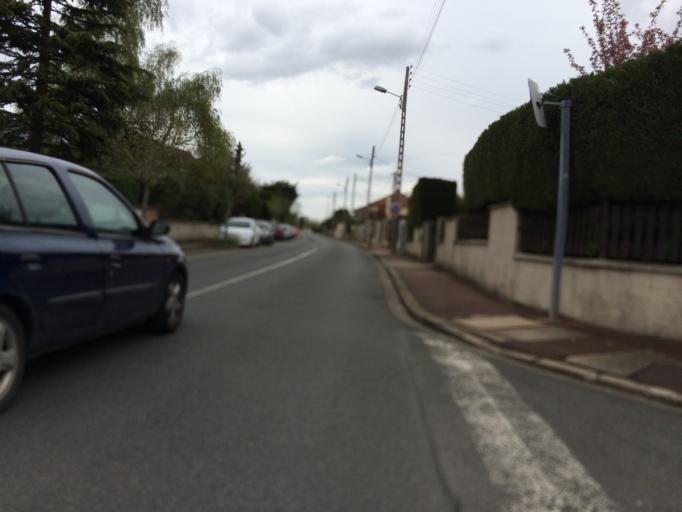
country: FR
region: Ile-de-France
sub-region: Departement de l'Essonne
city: Wissous
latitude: 48.7355
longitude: 2.3239
